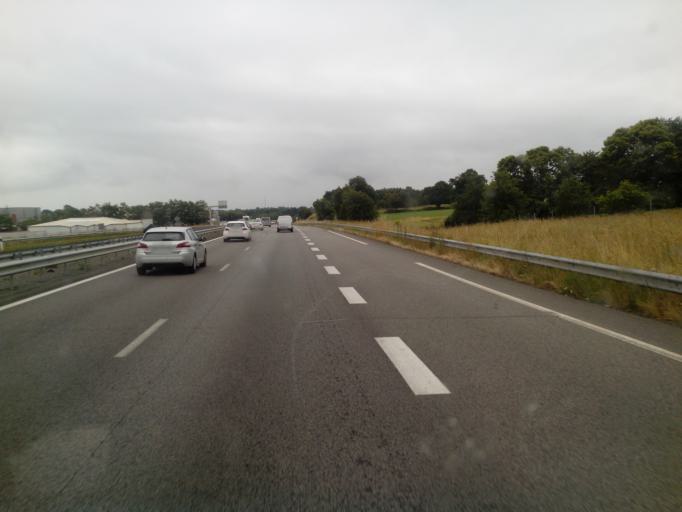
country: FR
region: Brittany
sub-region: Departement d'Ille-et-Vilaine
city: Laille
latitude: 47.9733
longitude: -1.6937
